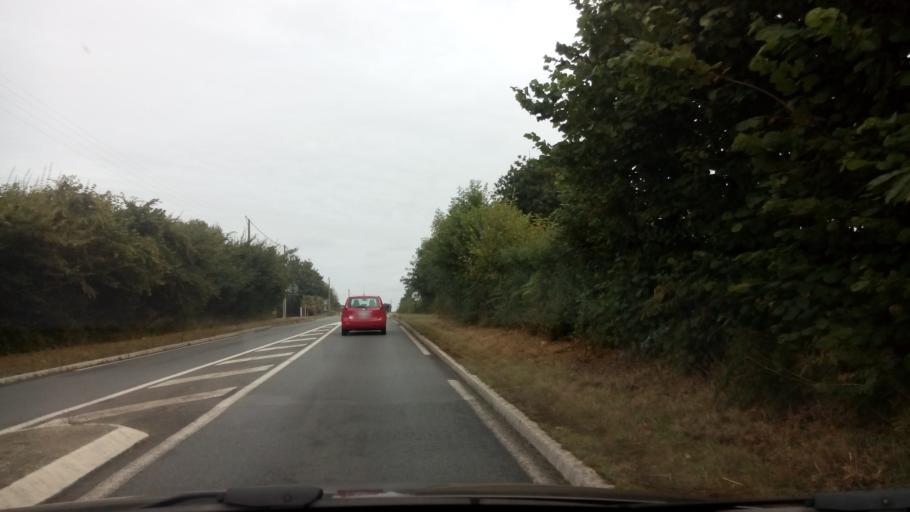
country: FR
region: Brittany
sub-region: Departement des Cotes-d'Armor
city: Ploumilliau
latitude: 48.7125
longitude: -3.4990
